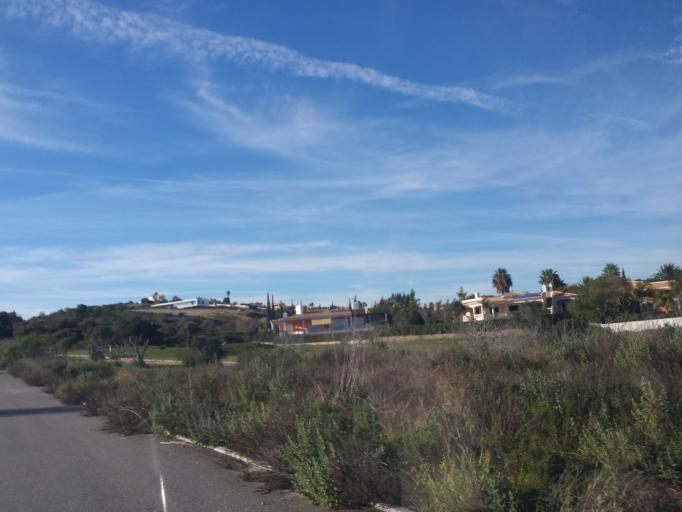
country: PT
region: Faro
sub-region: Portimao
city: Alvor
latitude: 37.1320
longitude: -8.6327
